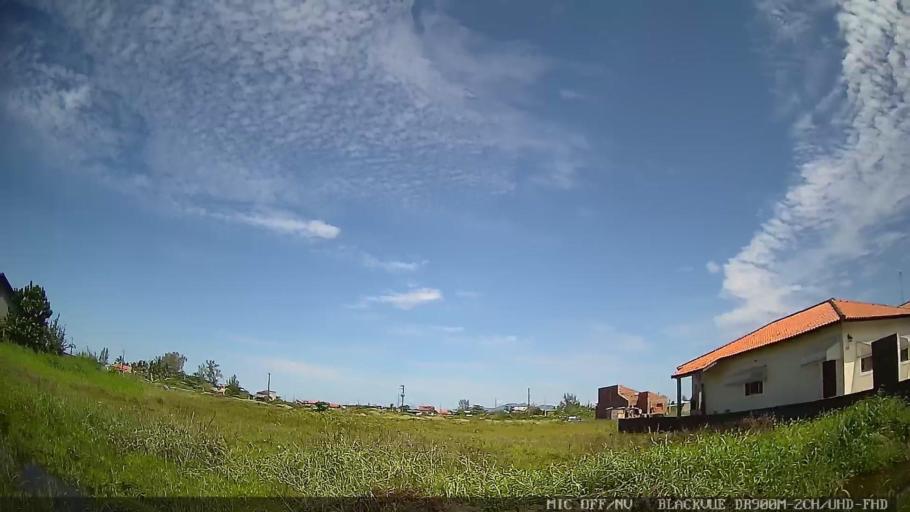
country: BR
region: Sao Paulo
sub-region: Iguape
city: Iguape
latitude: -24.7995
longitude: -47.6305
